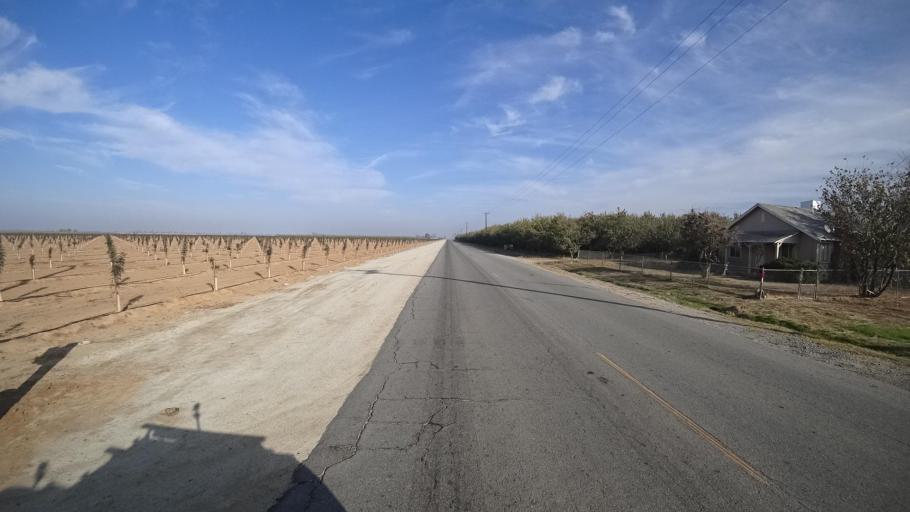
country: US
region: California
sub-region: Kern County
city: McFarland
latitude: 35.6530
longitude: -119.2046
